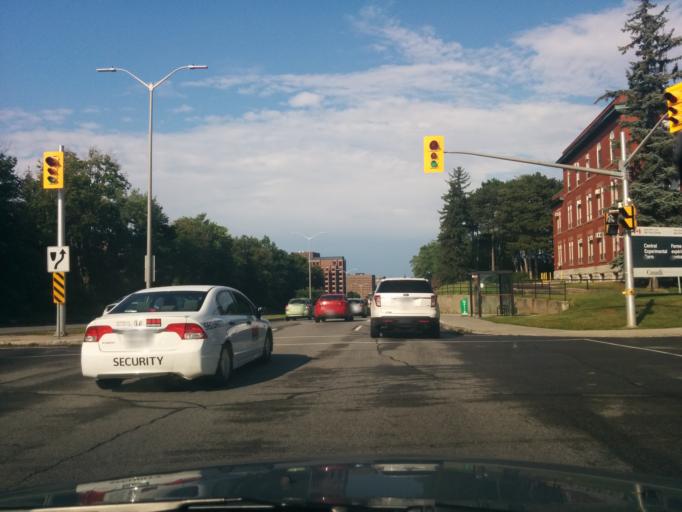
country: CA
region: Ontario
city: Ottawa
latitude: 45.3938
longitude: -75.7160
